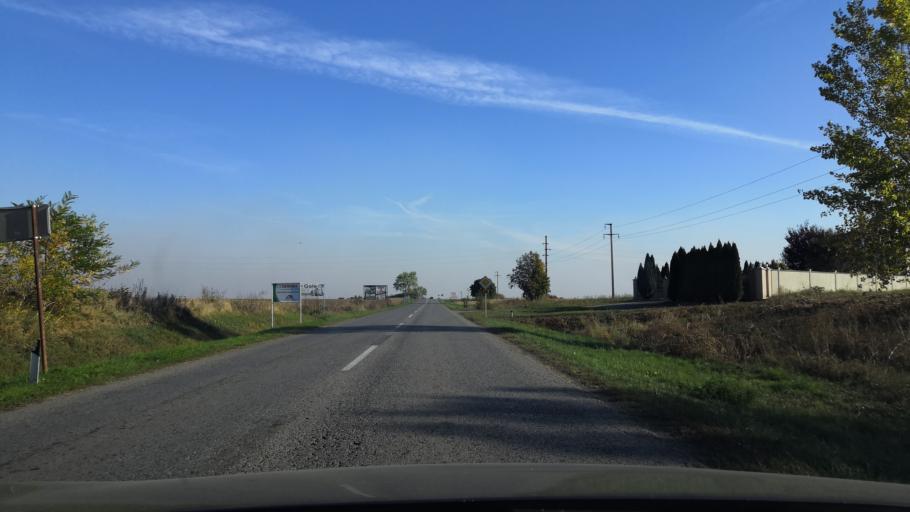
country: RS
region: Autonomna Pokrajina Vojvodina
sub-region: Sremski Okrug
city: Ruma
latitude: 45.0001
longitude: 19.8463
